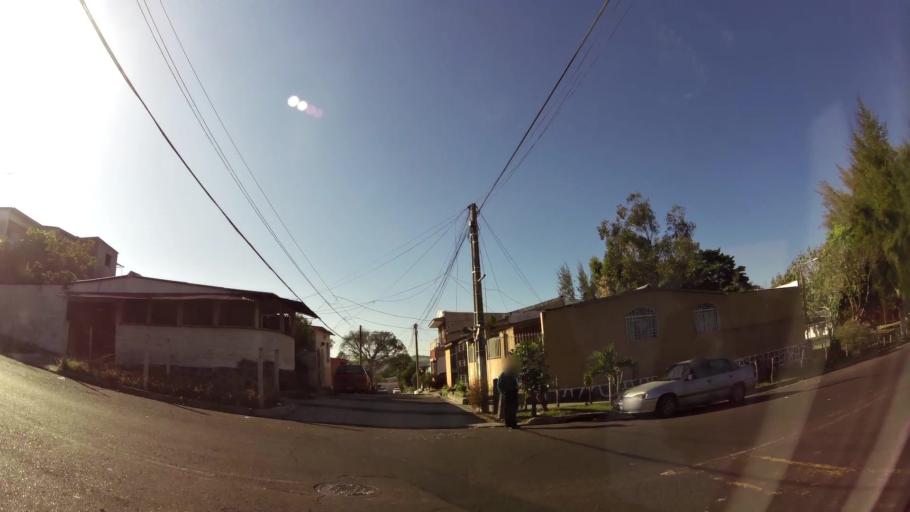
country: SV
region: La Libertad
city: Santa Tecla
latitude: 13.6910
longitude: -89.2903
